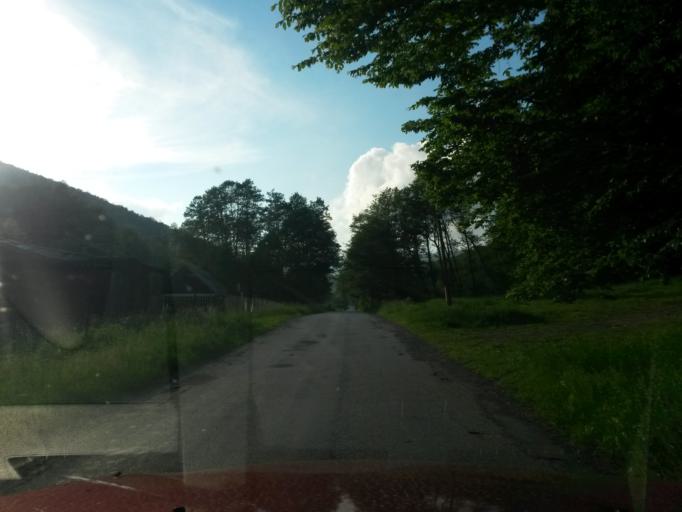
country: SK
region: Kosicky
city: Moldava nad Bodvou
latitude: 48.7353
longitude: 21.0289
